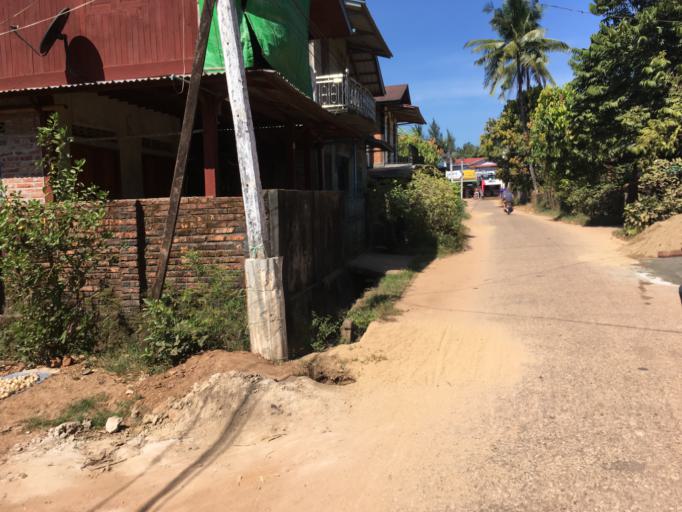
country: MM
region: Mon
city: Kyaikkami
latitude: 15.5083
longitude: 97.8554
